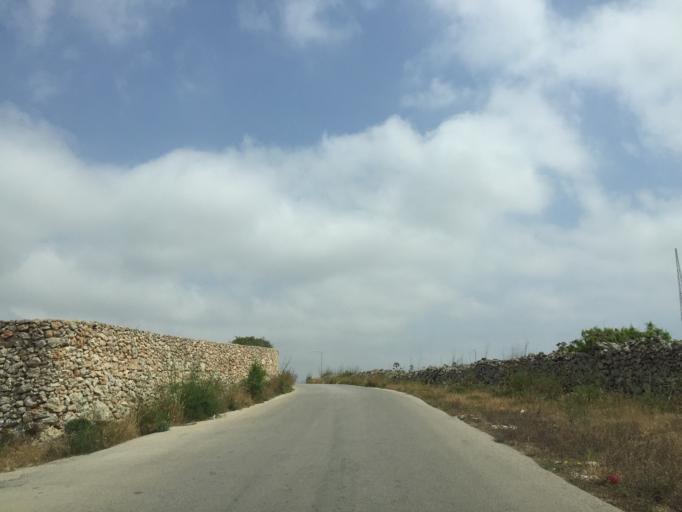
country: MT
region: L-Imgarr
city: Imgarr
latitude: 35.8943
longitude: 14.3595
